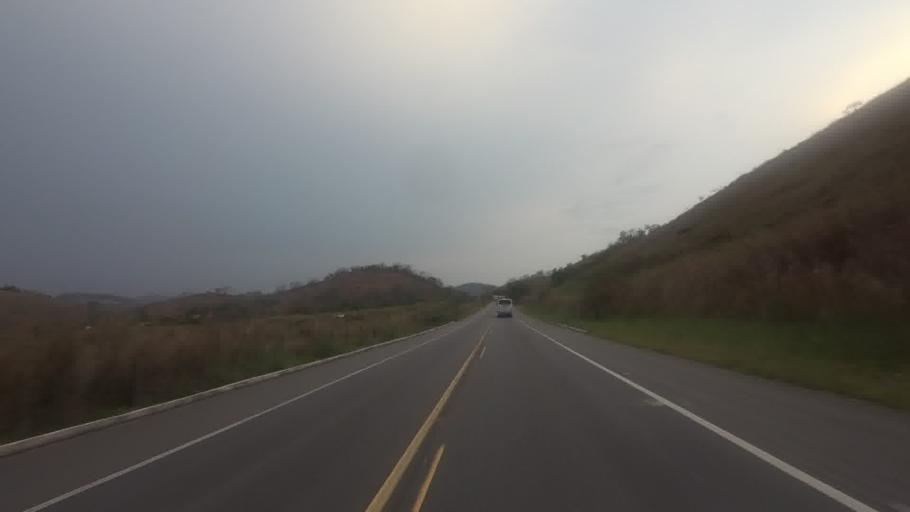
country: BR
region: Rio de Janeiro
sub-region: Carmo
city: Carmo
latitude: -21.8297
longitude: -42.6068
